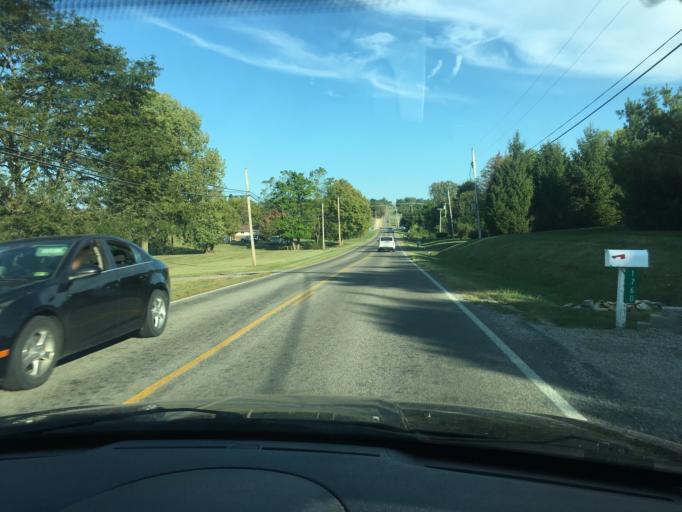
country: US
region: Ohio
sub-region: Logan County
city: Bellefontaine
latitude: 40.3503
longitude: -83.7306
